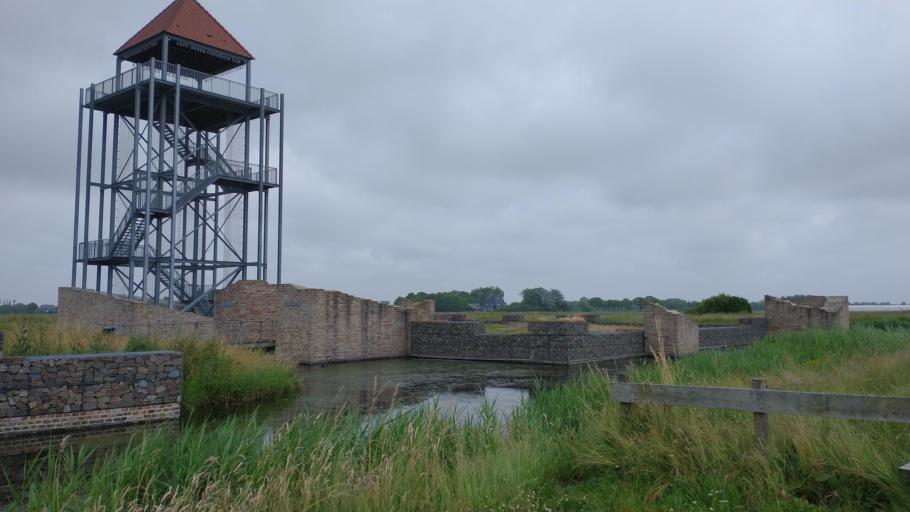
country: NL
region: North Holland
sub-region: Gemeente Schagen
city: Harenkarspel
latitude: 52.7356
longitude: 4.7101
